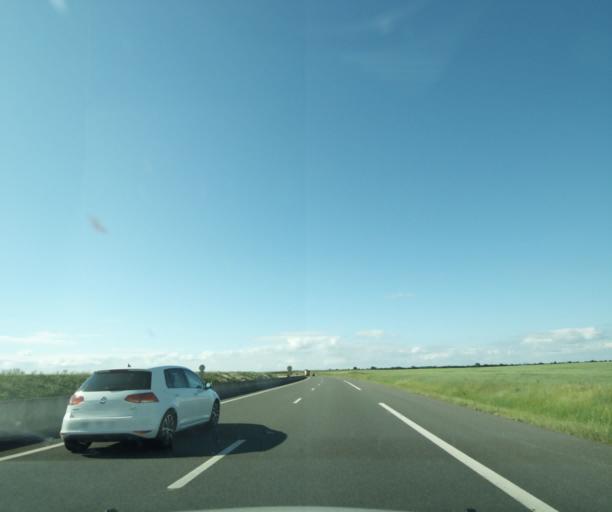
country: FR
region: Centre
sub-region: Departement d'Eure-et-Loir
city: Janville
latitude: 48.2589
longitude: 1.7634
